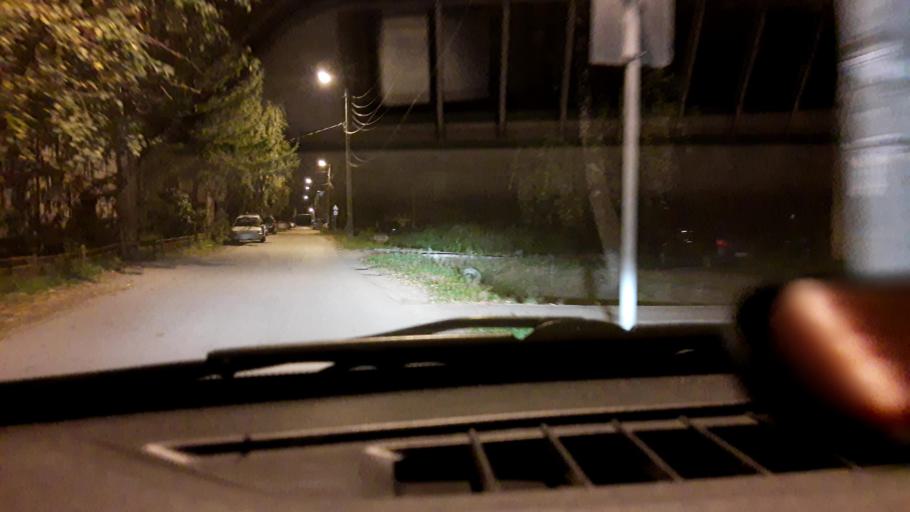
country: RU
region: Nizjnij Novgorod
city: Bor
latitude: 56.3482
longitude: 44.1903
